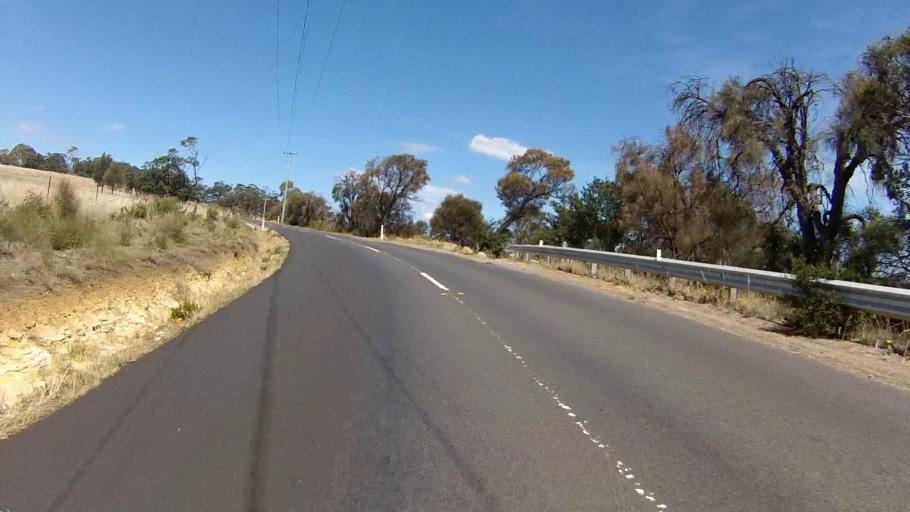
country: AU
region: Tasmania
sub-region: Sorell
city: Sorell
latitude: -42.7881
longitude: 147.5201
